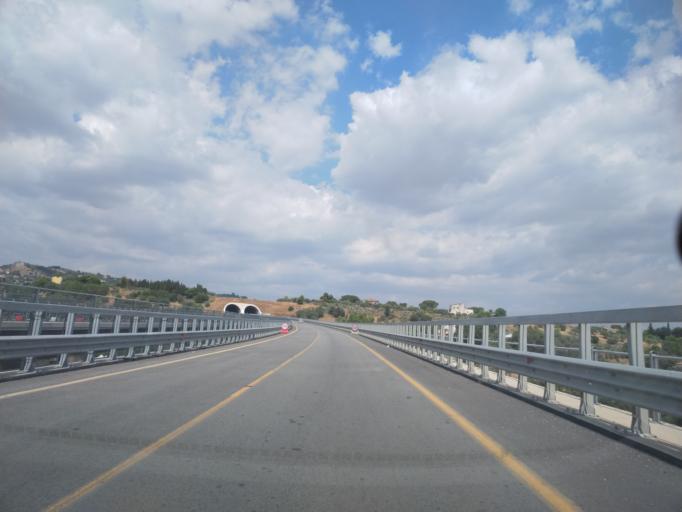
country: IT
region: Sicily
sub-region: Provincia di Caltanissetta
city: San Cataldo
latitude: 37.4639
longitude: 14.0036
